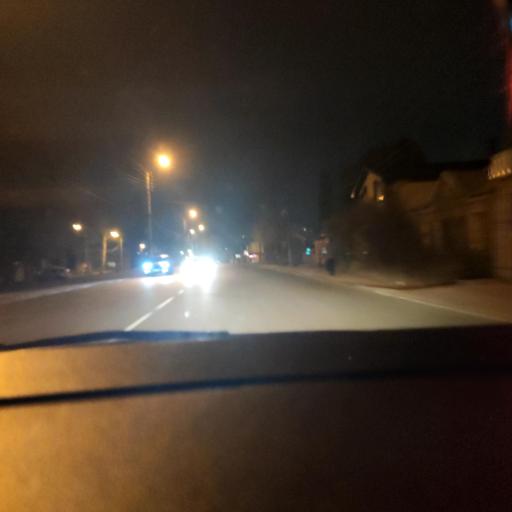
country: RU
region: Voronezj
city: Voronezh
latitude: 51.6306
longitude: 39.1750
